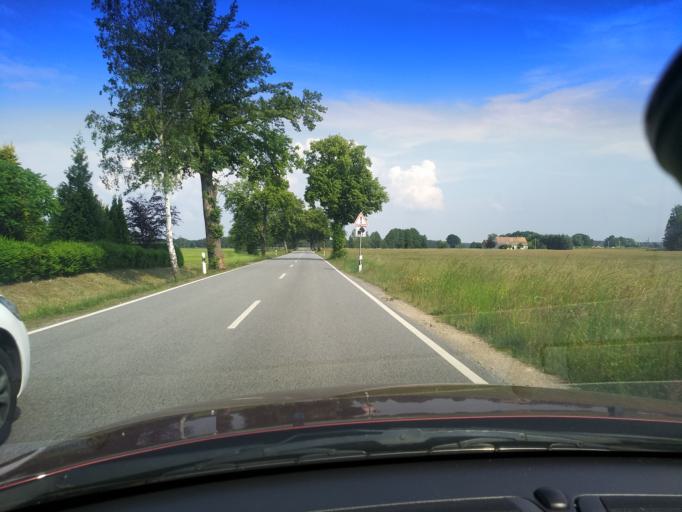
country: DE
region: Saxony
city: Klitten
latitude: 51.3481
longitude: 14.6061
